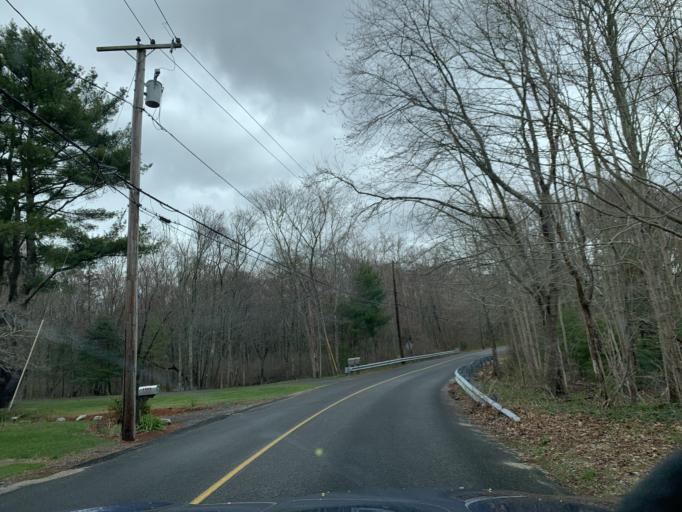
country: US
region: Massachusetts
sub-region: Bristol County
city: Rehoboth
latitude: 41.8976
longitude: -71.2188
